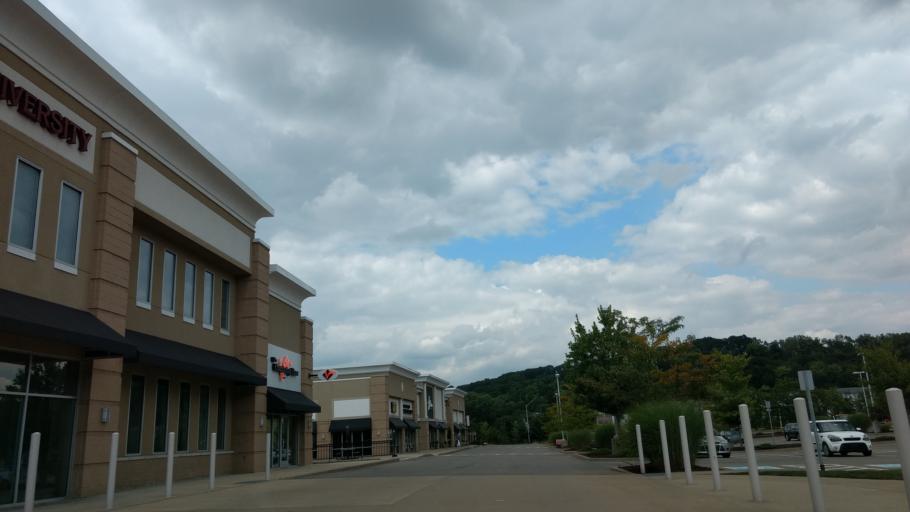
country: US
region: Pennsylvania
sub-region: Allegheny County
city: Bradford Woods
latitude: 40.6560
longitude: -80.0912
